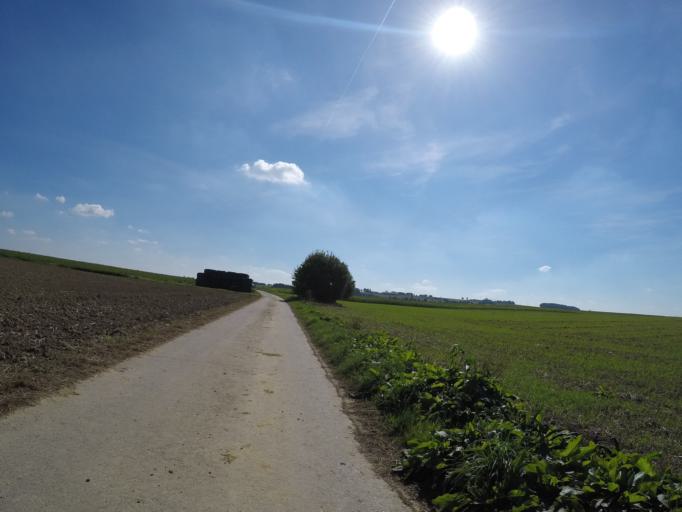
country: BE
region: Wallonia
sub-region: Province de Namur
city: Ciney
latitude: 50.3225
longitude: 5.0532
